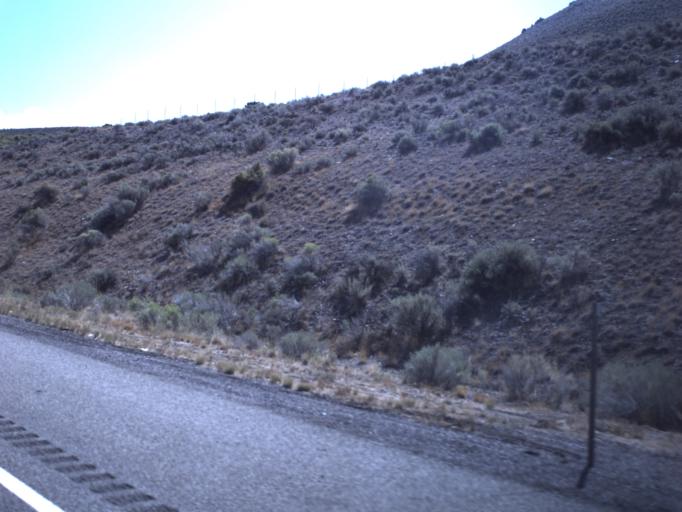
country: US
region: Utah
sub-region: Sevier County
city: Aurora
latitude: 38.8784
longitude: -111.9347
